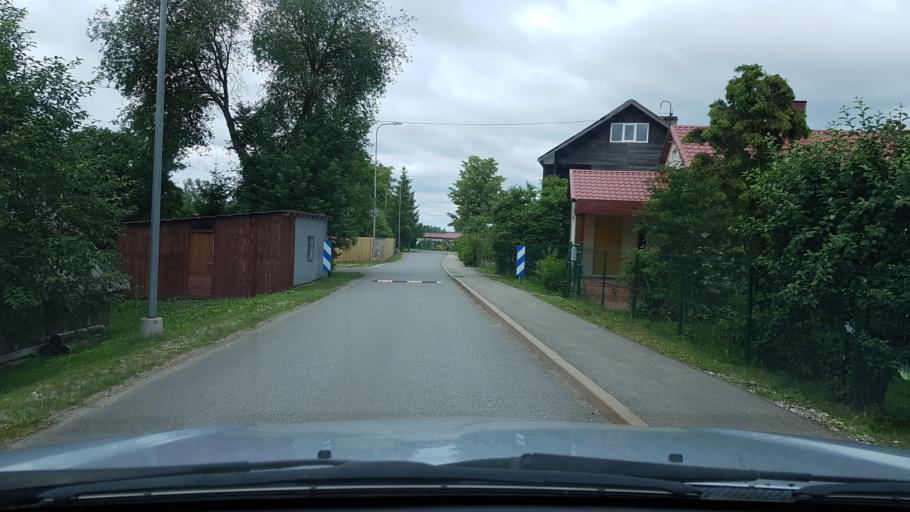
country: EE
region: Ida-Virumaa
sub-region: Narva linn
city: Narva
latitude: 59.3957
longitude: 28.1243
